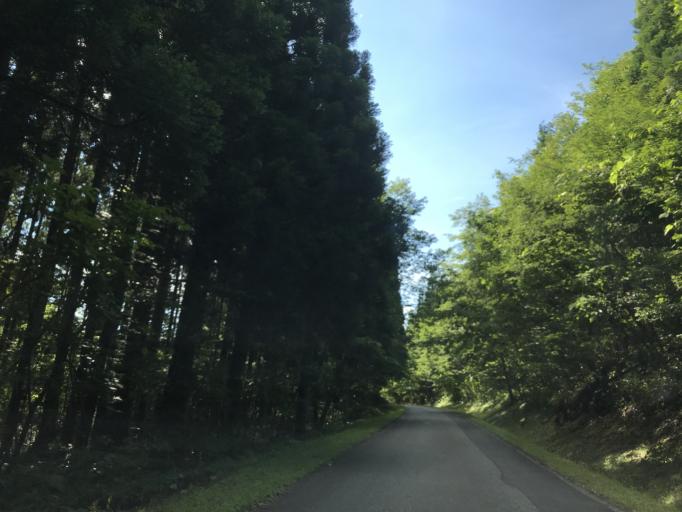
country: JP
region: Iwate
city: Ichinoseki
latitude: 38.9262
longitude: 140.9362
